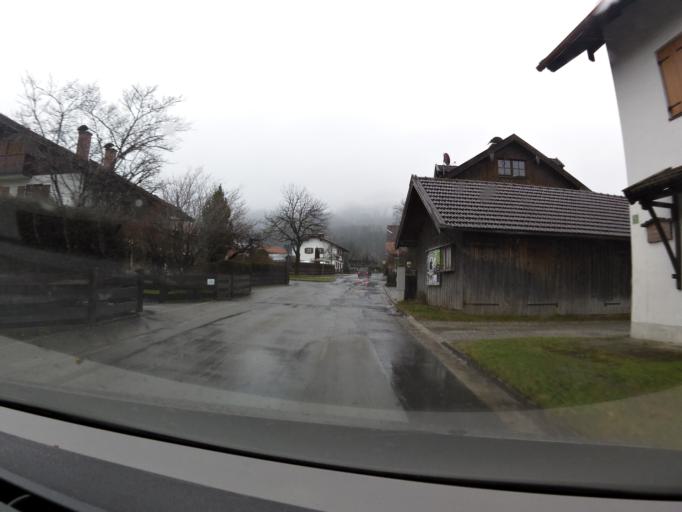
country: DE
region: Bavaria
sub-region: Upper Bavaria
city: Benediktbeuern
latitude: 47.7000
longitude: 11.4149
